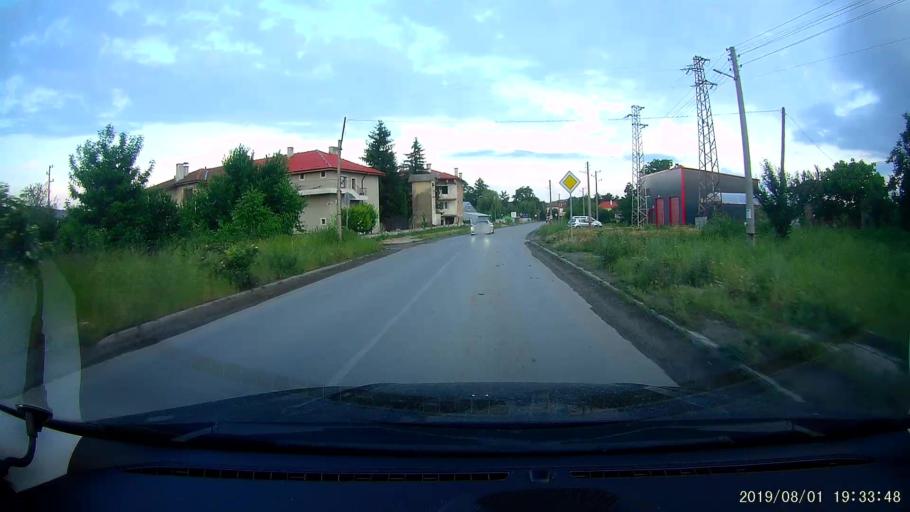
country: BG
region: Burgas
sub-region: Obshtina Sungurlare
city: Sungurlare
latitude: 42.7757
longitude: 26.8776
